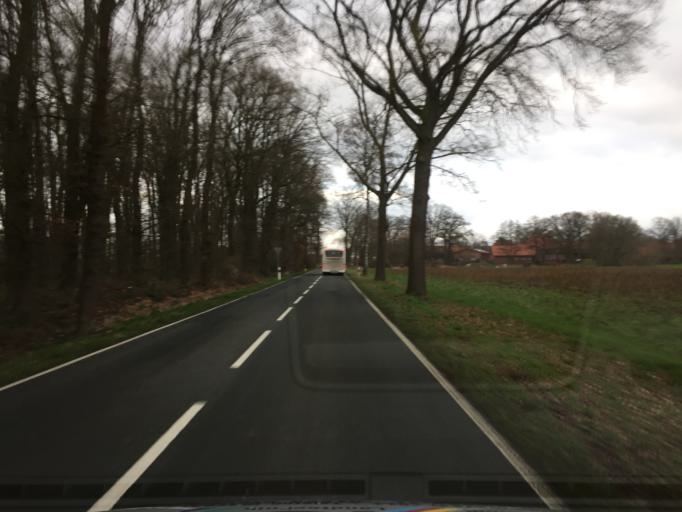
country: DE
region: Lower Saxony
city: Steyerberg
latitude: 52.5317
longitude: 9.0270
